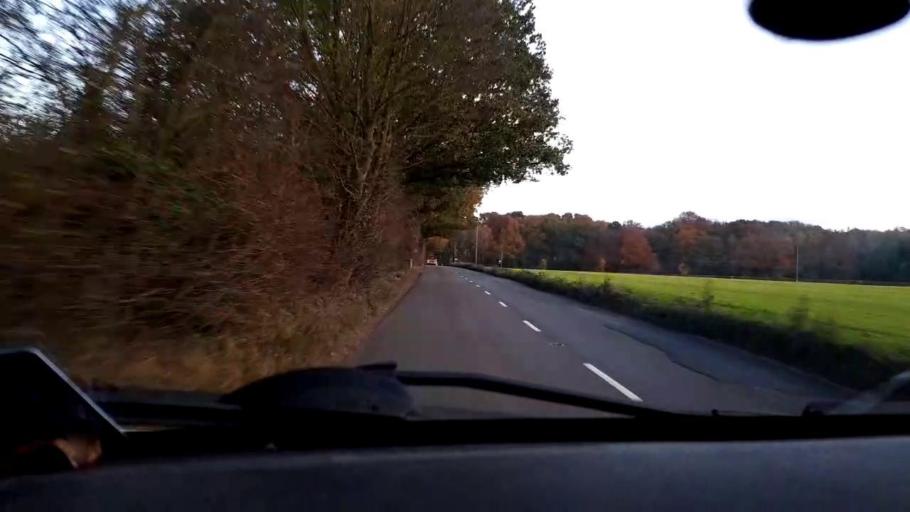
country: GB
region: England
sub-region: Norfolk
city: Mattishall
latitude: 52.6819
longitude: 1.1050
